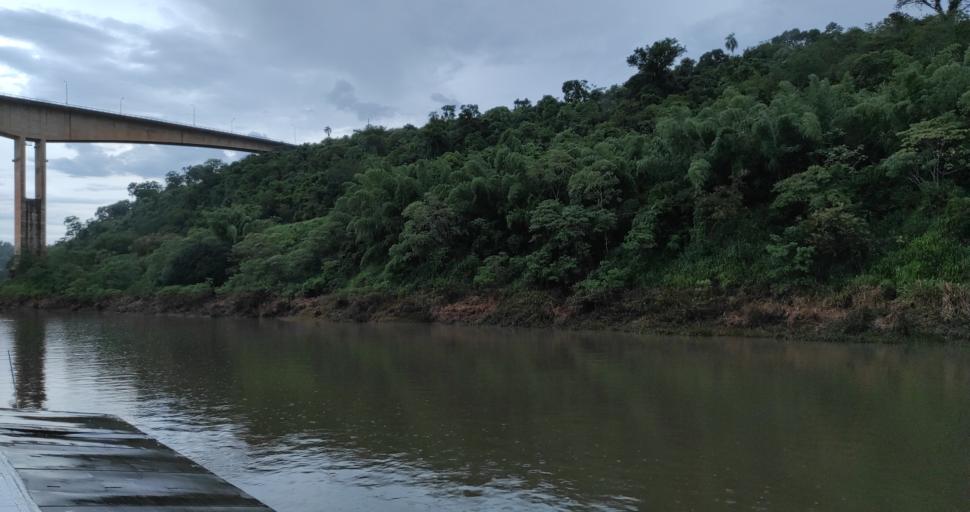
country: AR
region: Misiones
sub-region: Departamento de Iguazu
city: Puerto Iguazu
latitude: -25.5905
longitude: -54.5640
